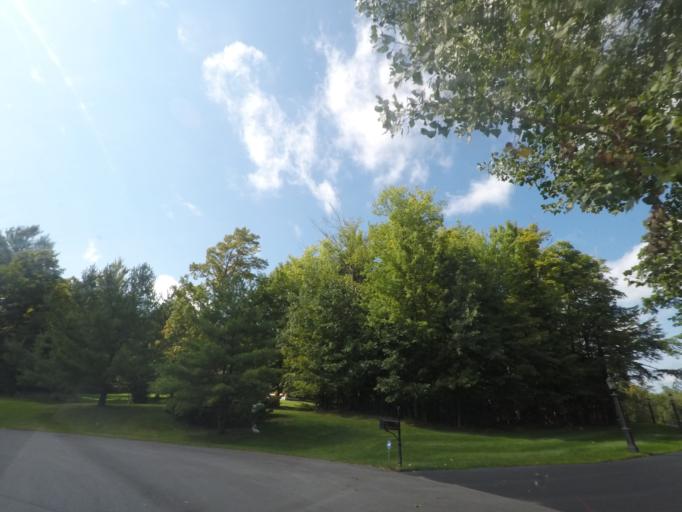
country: US
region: New York
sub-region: Rensselaer County
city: West Sand Lake
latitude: 42.5970
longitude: -73.6247
